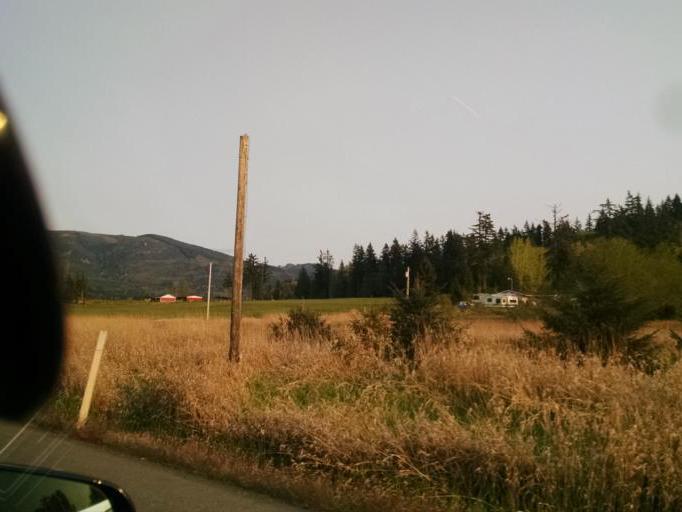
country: US
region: Washington
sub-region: Whatcom County
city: Geneva
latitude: 48.8039
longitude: -122.3674
